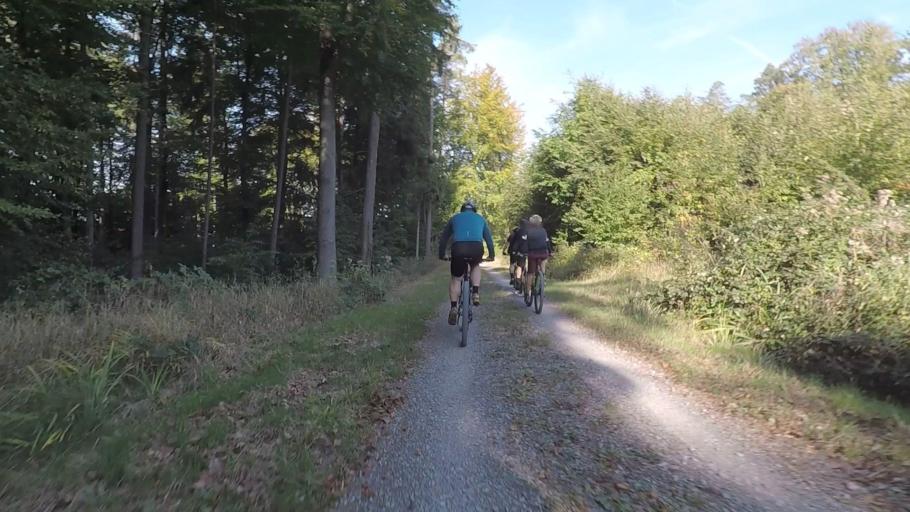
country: DE
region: Baden-Wuerttemberg
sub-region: Regierungsbezirk Stuttgart
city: Wustenrot
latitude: 49.0634
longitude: 9.4644
